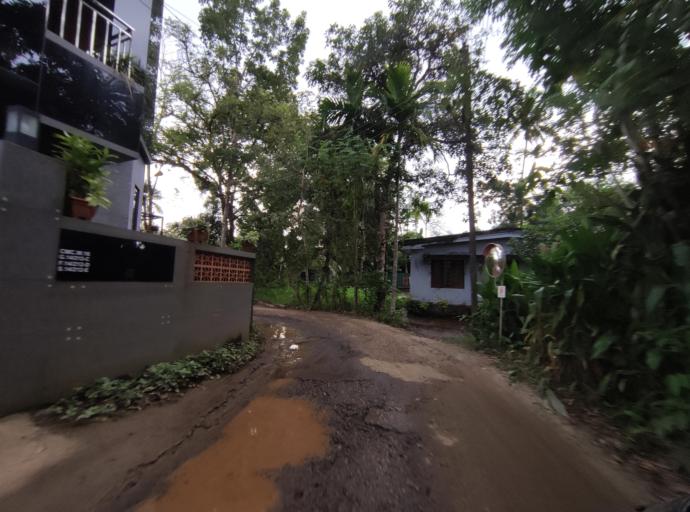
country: IN
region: Kerala
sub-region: Alappuzha
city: Shertallai
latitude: 9.6693
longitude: 76.3415
